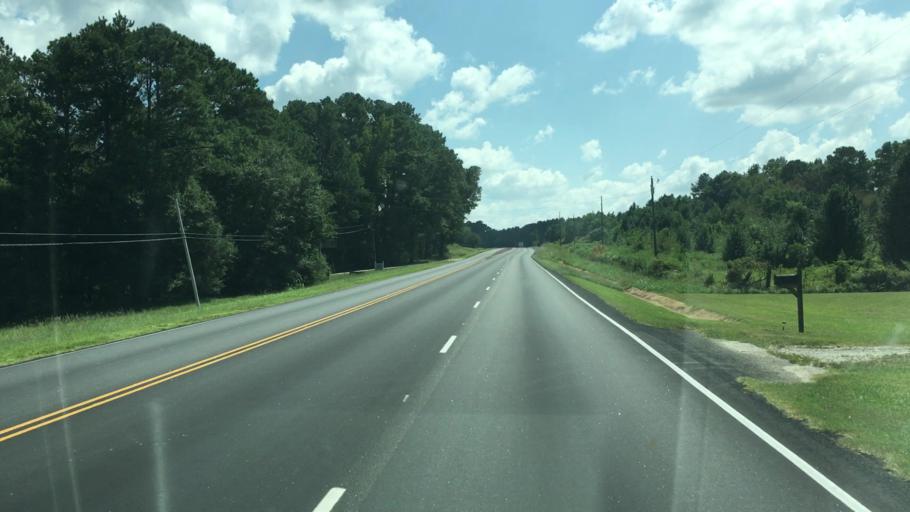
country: US
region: Georgia
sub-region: Morgan County
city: Madison
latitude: 33.6388
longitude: -83.4497
